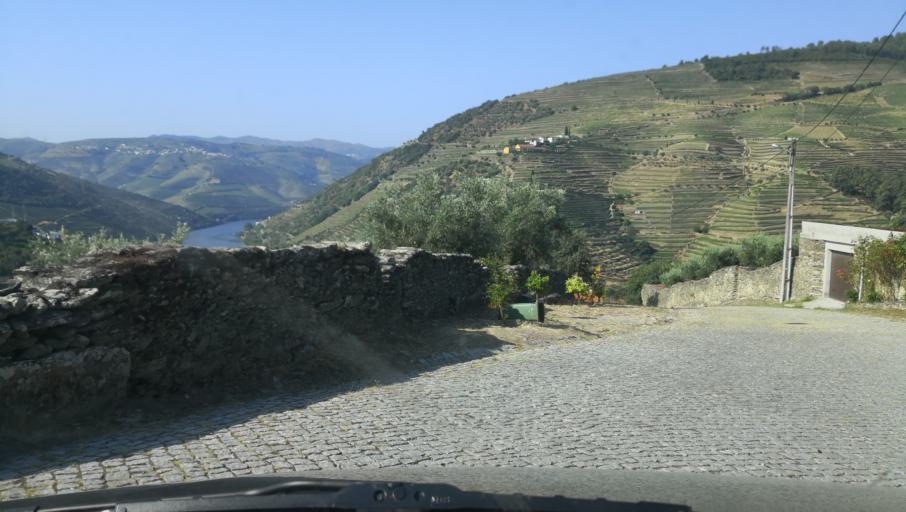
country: PT
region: Vila Real
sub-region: Sabrosa
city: Vilela
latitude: 41.2004
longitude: -7.5459
